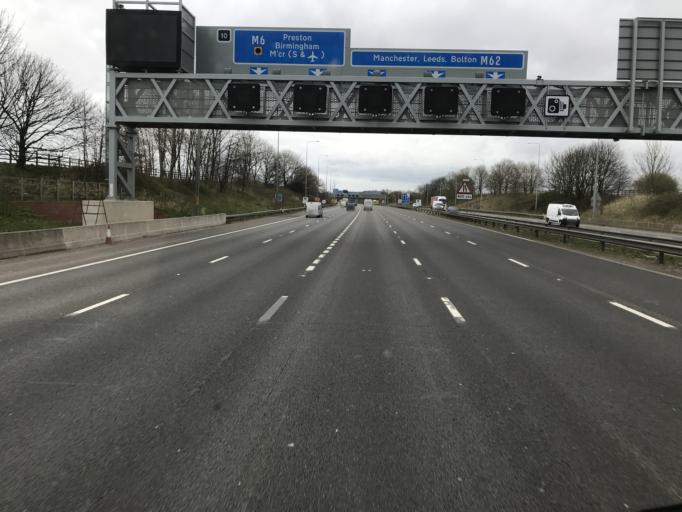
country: GB
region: England
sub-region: Warrington
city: Winwick
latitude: 53.4229
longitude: -2.5847
